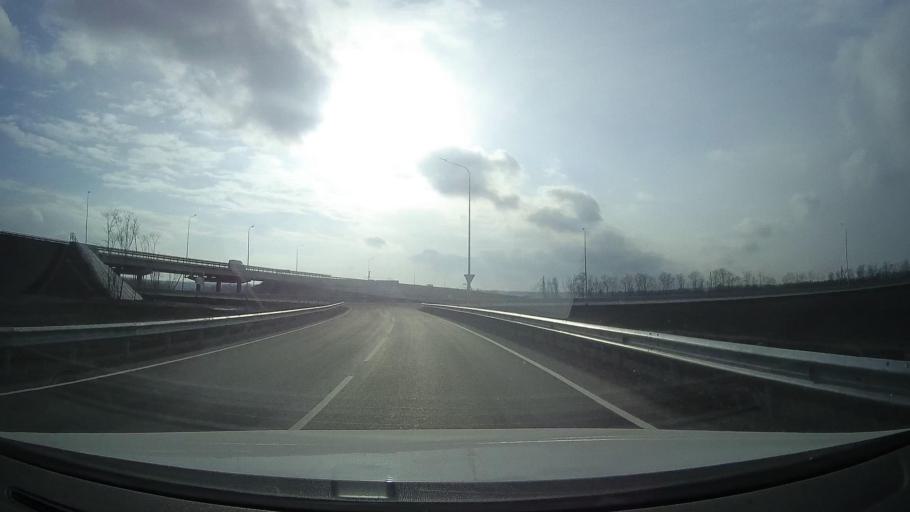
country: RU
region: Rostov
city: Grushevskaya
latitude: 47.4555
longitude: 39.8823
